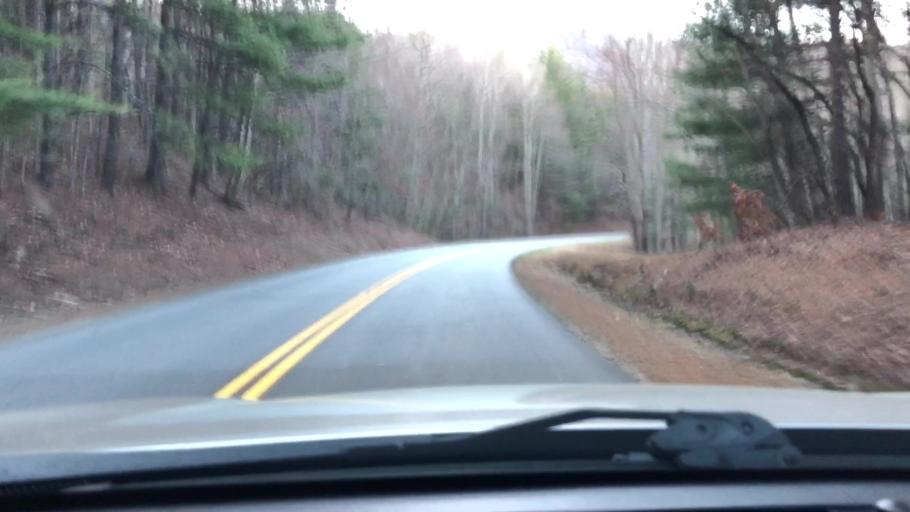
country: US
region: North Carolina
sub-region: Buncombe County
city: Biltmore Forest
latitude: 35.5426
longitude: -82.4986
